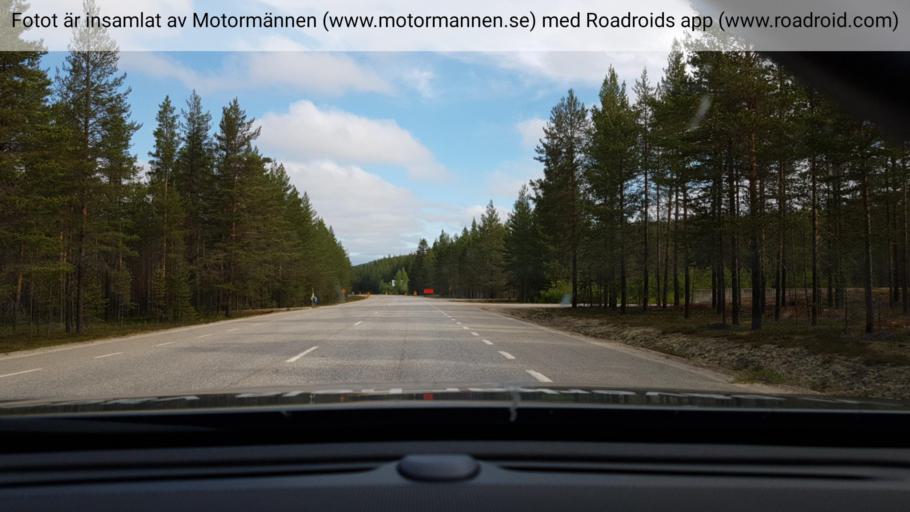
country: SE
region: Vaesterbotten
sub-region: Norsjo Kommun
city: Norsjoe
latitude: 64.6018
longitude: 19.2982
